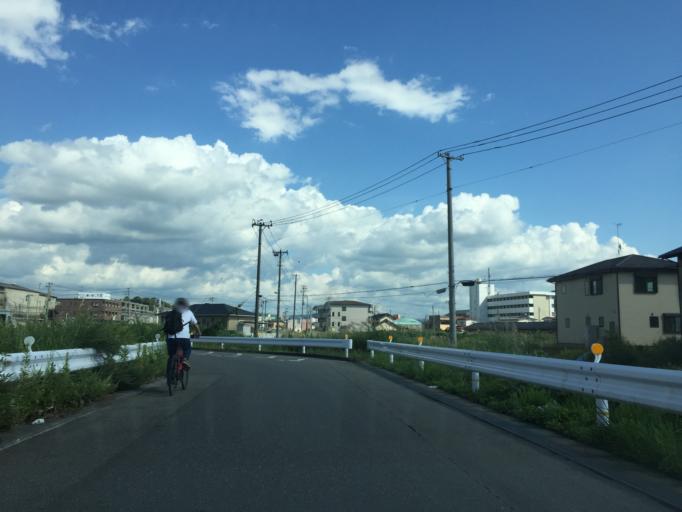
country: JP
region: Fukushima
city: Koriyama
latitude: 37.4127
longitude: 140.3758
